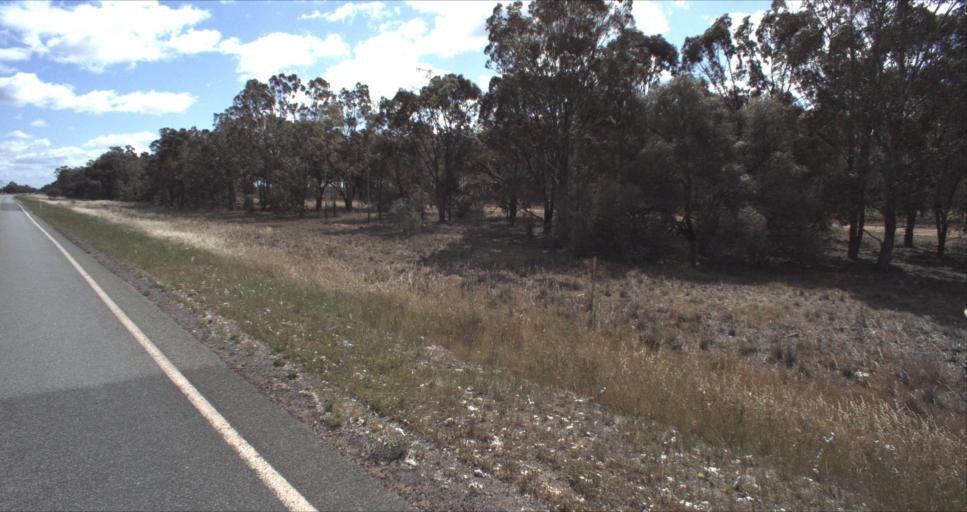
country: AU
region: New South Wales
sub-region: Murrumbidgee Shire
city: Darlington Point
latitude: -34.5841
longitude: 146.1646
